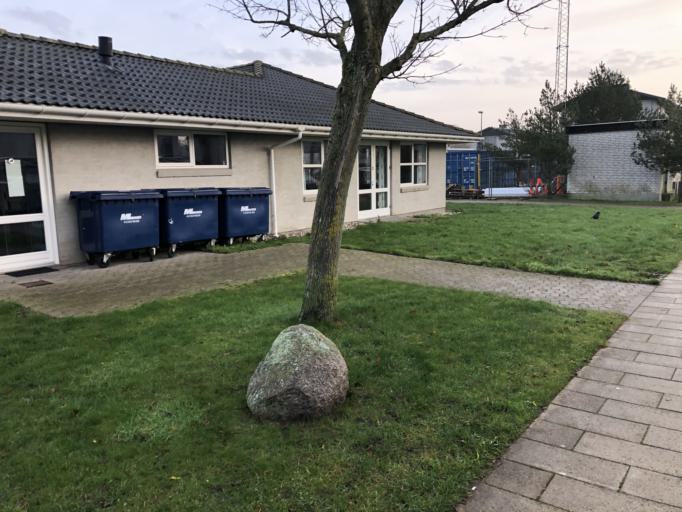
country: DK
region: Capital Region
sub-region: Helsingor Kommune
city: Espergaerde
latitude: 56.0152
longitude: 12.5788
